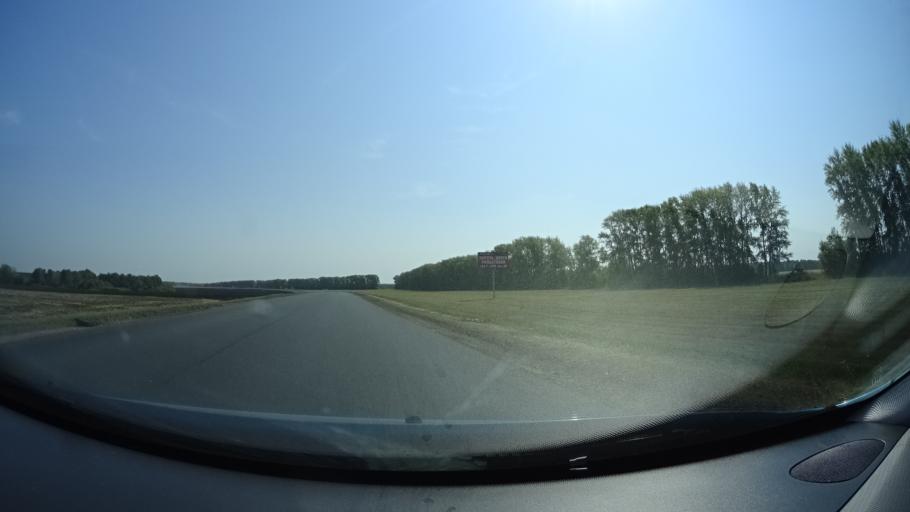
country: RU
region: Bashkortostan
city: Karmaskaly
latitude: 54.3879
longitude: 56.1324
